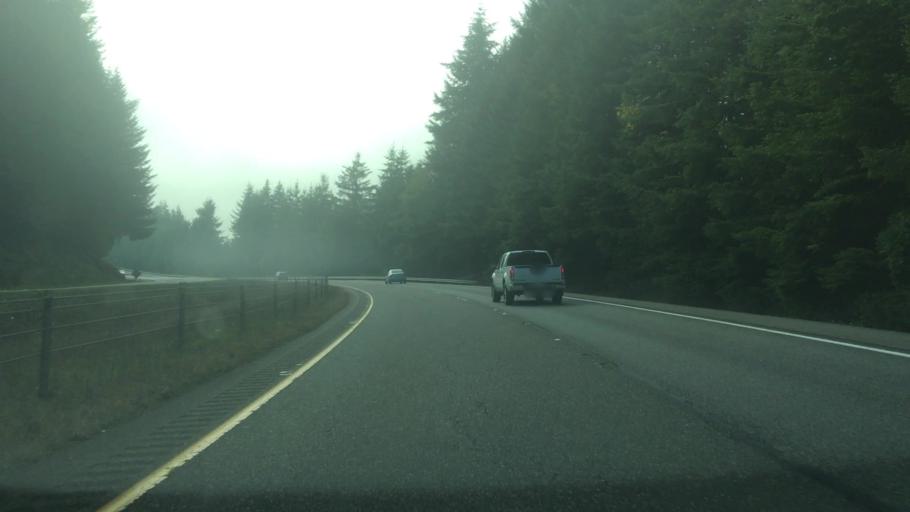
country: US
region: Washington
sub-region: Grays Harbor County
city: McCleary
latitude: 47.0381
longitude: -123.3320
